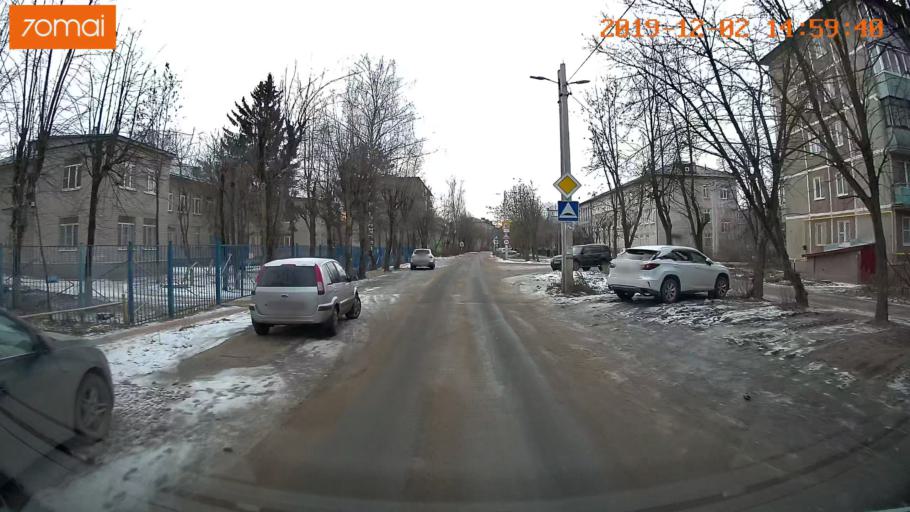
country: RU
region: Ivanovo
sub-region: Gorod Ivanovo
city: Ivanovo
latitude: 56.9717
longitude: 41.0091
